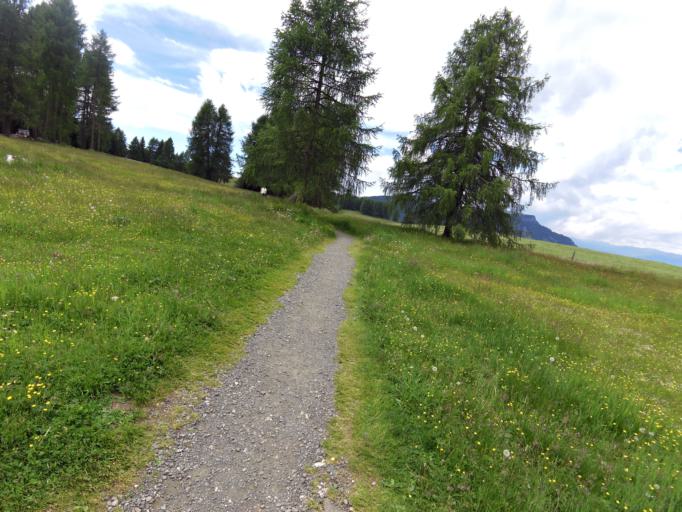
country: IT
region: Trentino-Alto Adige
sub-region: Bolzano
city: Ortisei
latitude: 46.5363
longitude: 11.6466
